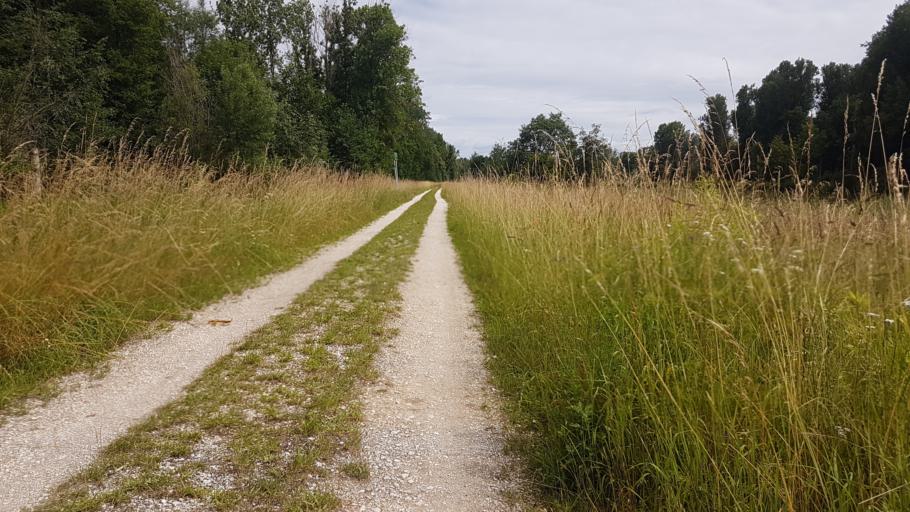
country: DE
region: Bavaria
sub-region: Swabia
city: Gundremmingen
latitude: 48.5278
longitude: 10.3881
